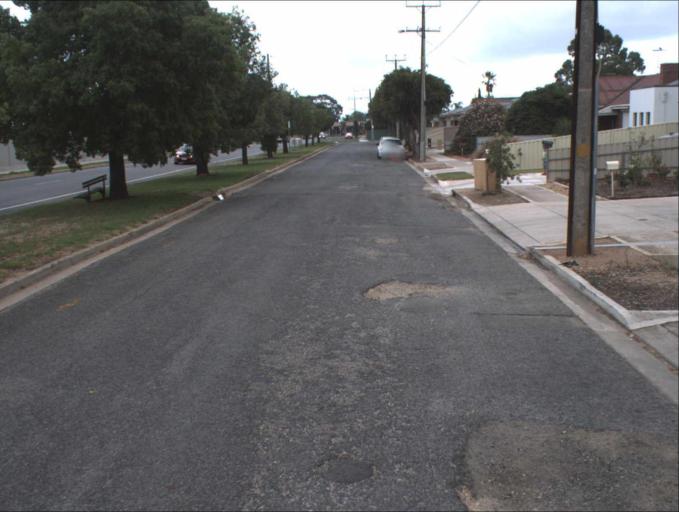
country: AU
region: South Australia
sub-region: Port Adelaide Enfield
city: Enfield
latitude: -34.8585
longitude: 138.6208
